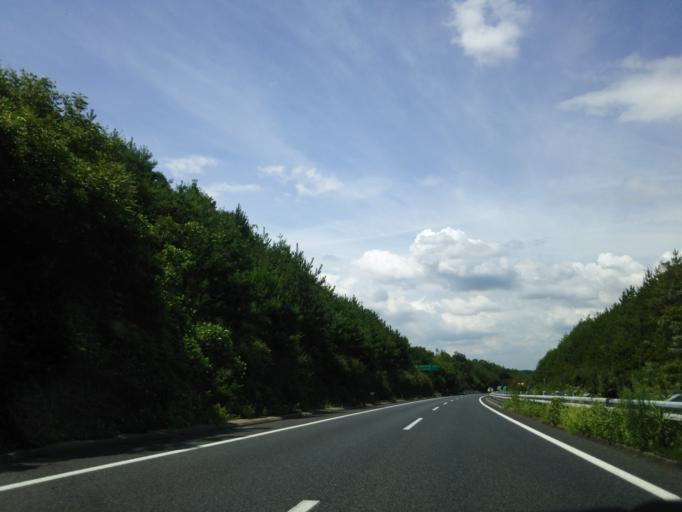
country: JP
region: Gifu
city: Toki
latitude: 35.3120
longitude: 137.1777
